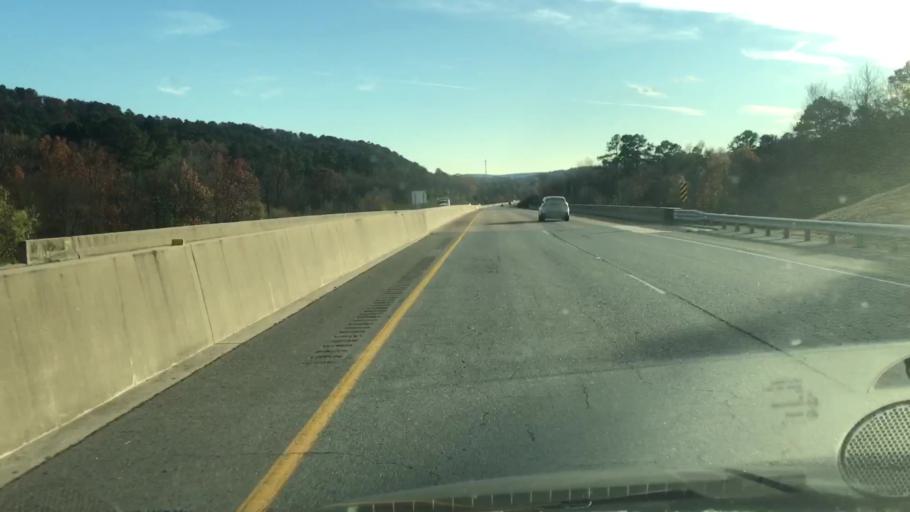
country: US
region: Arkansas
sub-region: Garland County
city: Hot Springs
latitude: 34.4864
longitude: -92.9808
